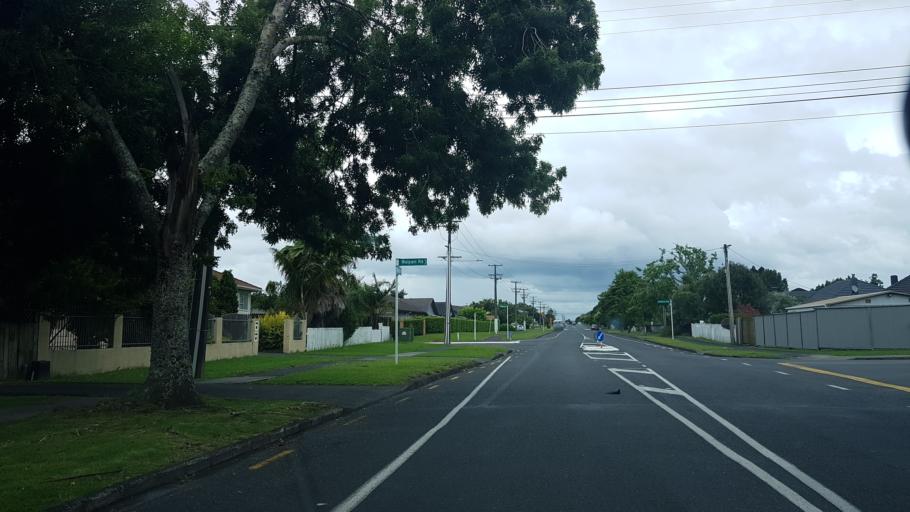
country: NZ
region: Auckland
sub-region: Auckland
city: Rosebank
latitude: -36.8334
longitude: 174.6564
